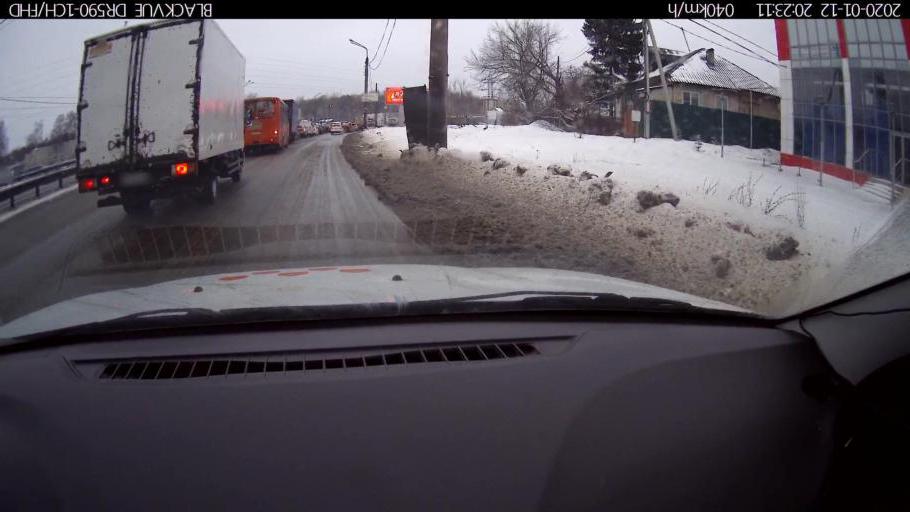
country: RU
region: Nizjnij Novgorod
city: Nizhniy Novgorod
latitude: 56.2842
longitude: 43.8922
